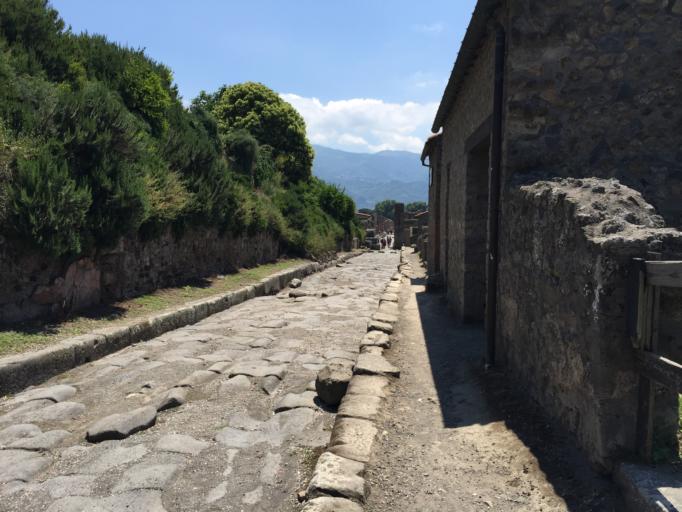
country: IT
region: Campania
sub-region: Provincia di Napoli
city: Pompei
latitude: 40.7529
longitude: 14.4848
